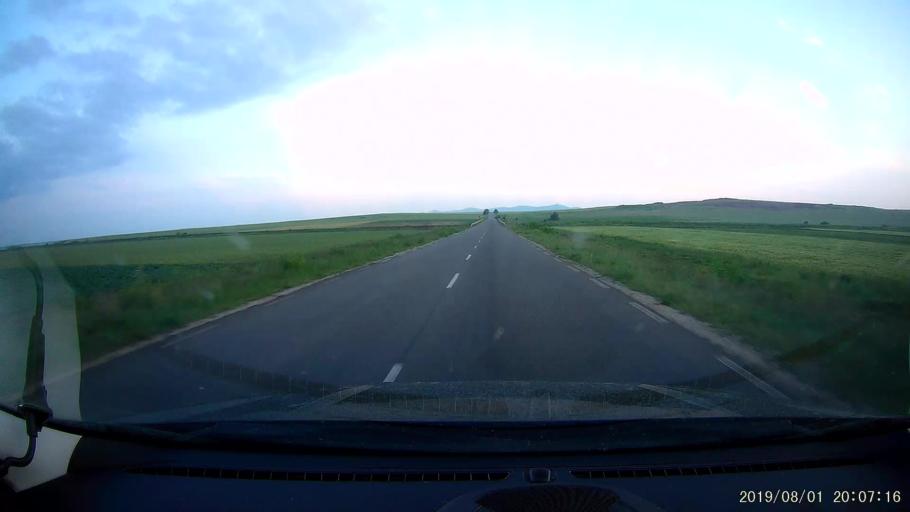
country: BG
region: Yambol
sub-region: Obshtina Yambol
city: Yambol
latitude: 42.5249
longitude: 26.5660
